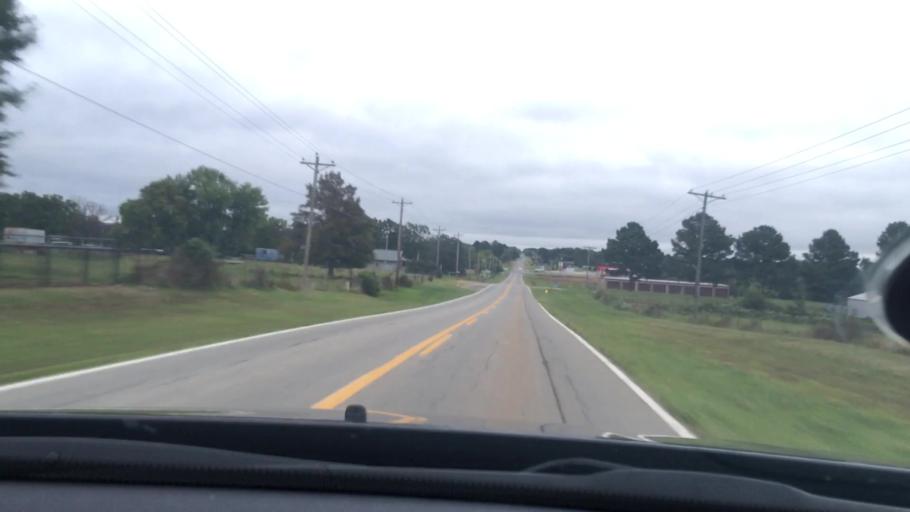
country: US
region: Oklahoma
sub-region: Sequoyah County
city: Vian
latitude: 35.6097
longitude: -94.9826
